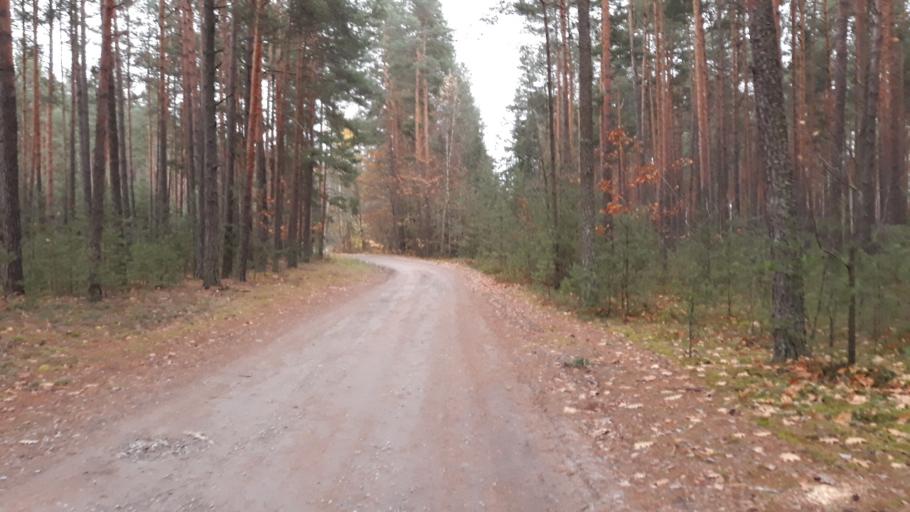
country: PL
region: Lublin Voivodeship
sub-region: Powiat janowski
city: Dzwola
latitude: 50.6535
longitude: 22.5729
